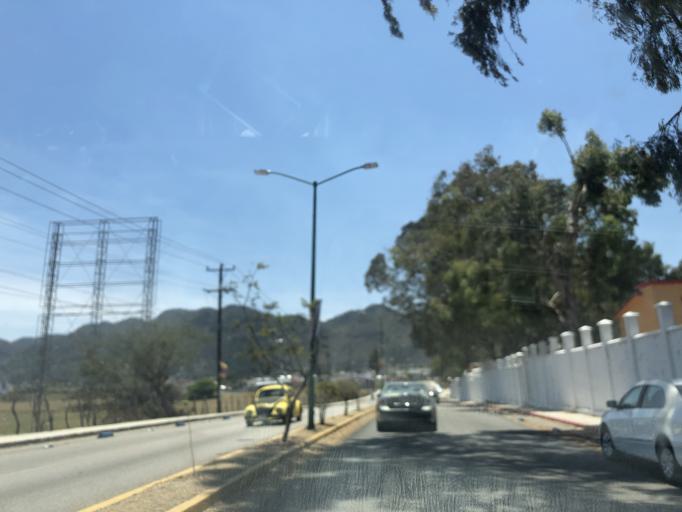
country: MX
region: Chiapas
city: San Cristobal de las Casas
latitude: 16.7254
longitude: -92.6515
